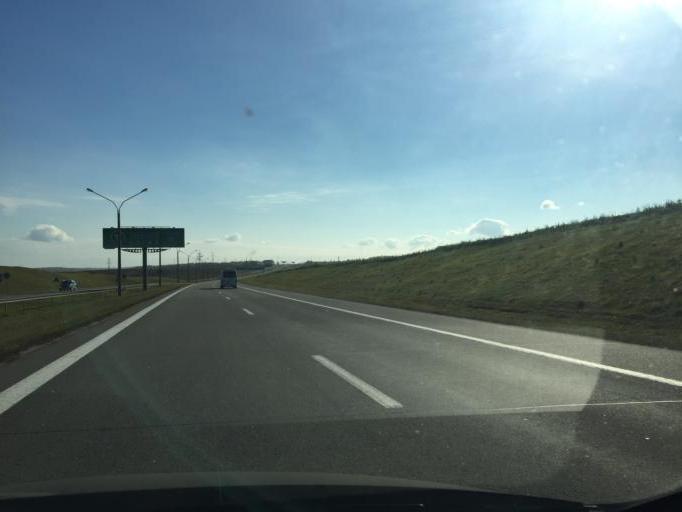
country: BY
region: Minsk
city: Slabada
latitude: 54.0081
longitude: 27.9029
